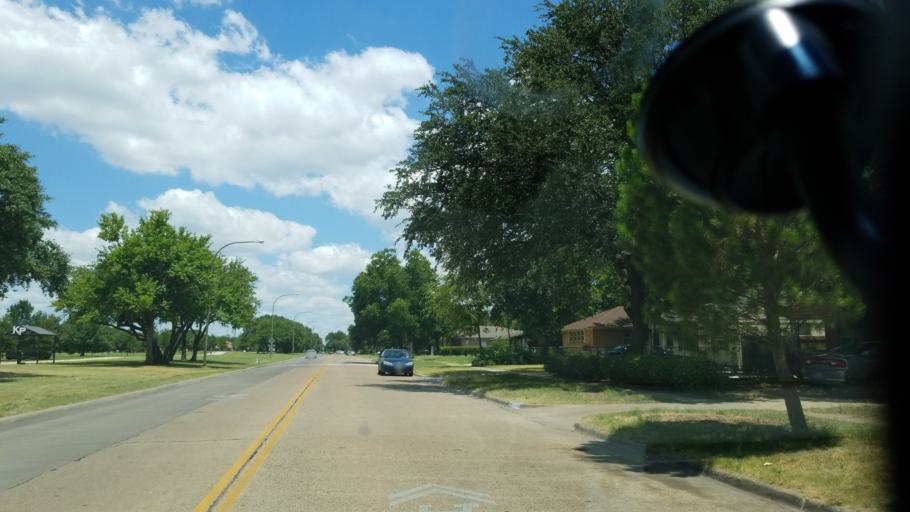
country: US
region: Texas
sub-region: Dallas County
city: Cockrell Hill
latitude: 32.7103
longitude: -96.8486
